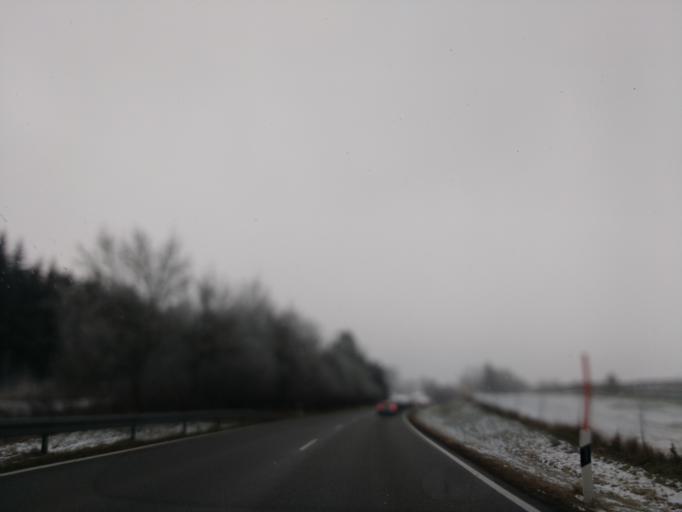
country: DE
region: Bavaria
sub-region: Swabia
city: Oy-Mittelberg
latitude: 47.6407
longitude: 10.4693
